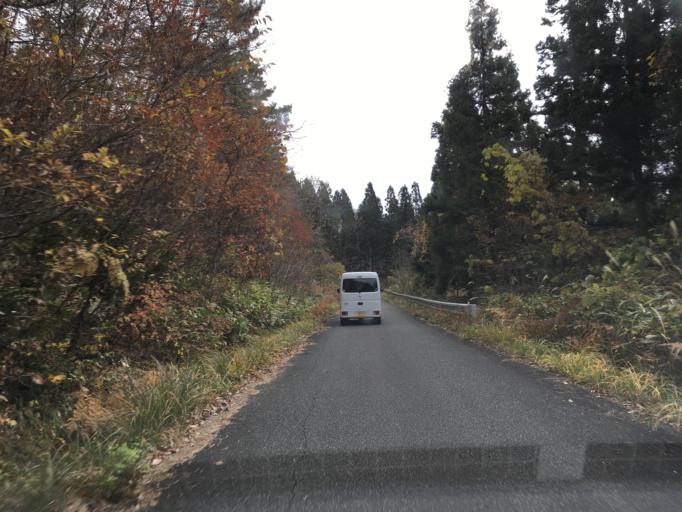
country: JP
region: Iwate
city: Mizusawa
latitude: 39.1249
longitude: 141.3206
